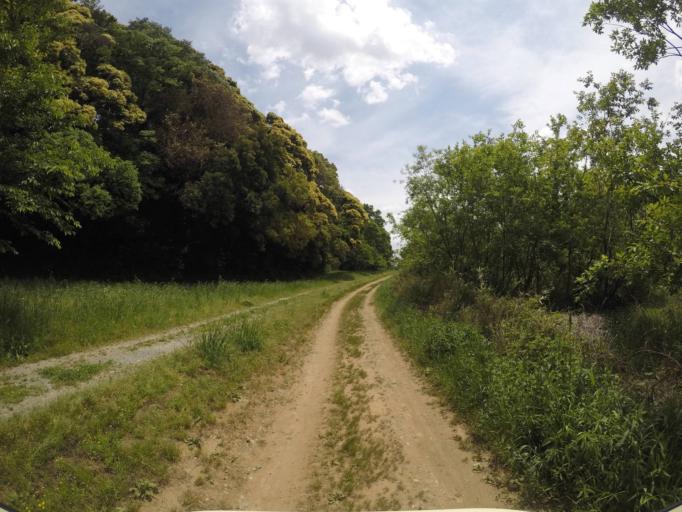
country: JP
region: Ibaraki
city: Ushiku
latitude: 35.9552
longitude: 140.1277
